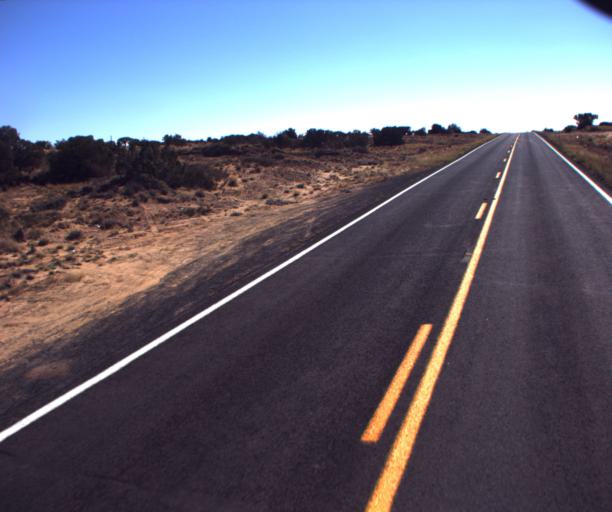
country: US
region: Arizona
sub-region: Coconino County
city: Tuba City
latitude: 35.9398
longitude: -110.8528
